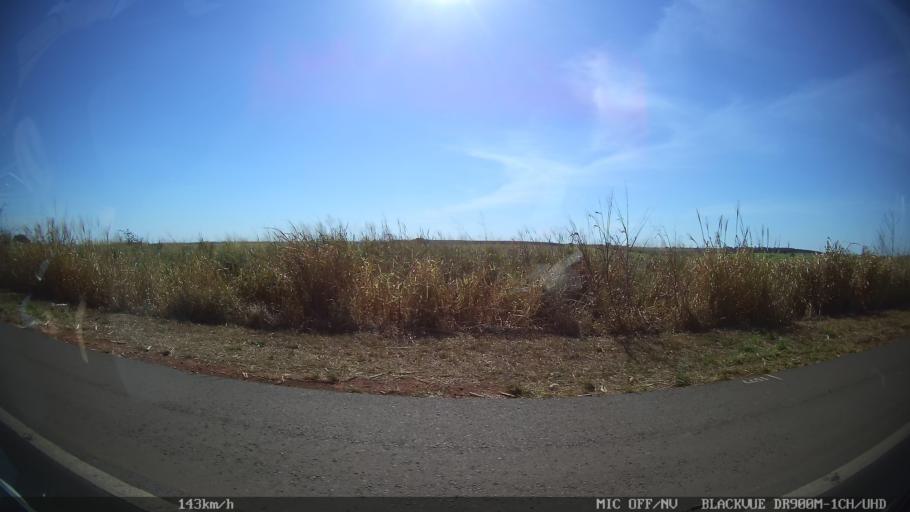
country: BR
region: Sao Paulo
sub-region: Olimpia
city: Olimpia
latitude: -20.6800
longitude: -48.8946
